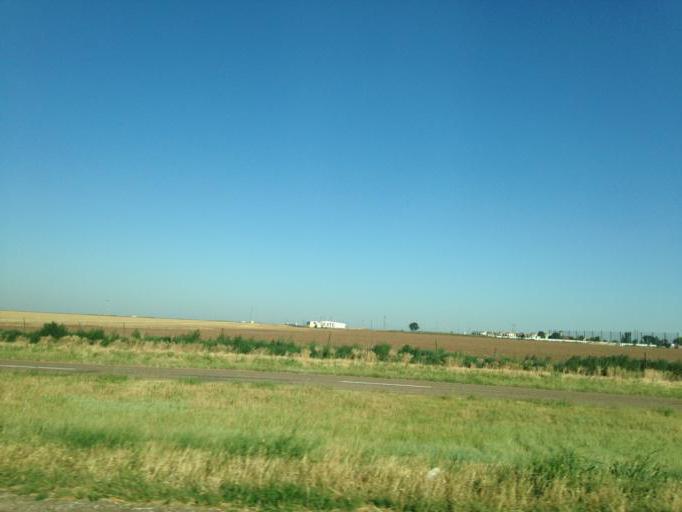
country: US
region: Texas
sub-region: Randall County
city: Canyon
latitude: 35.1094
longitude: -101.9115
